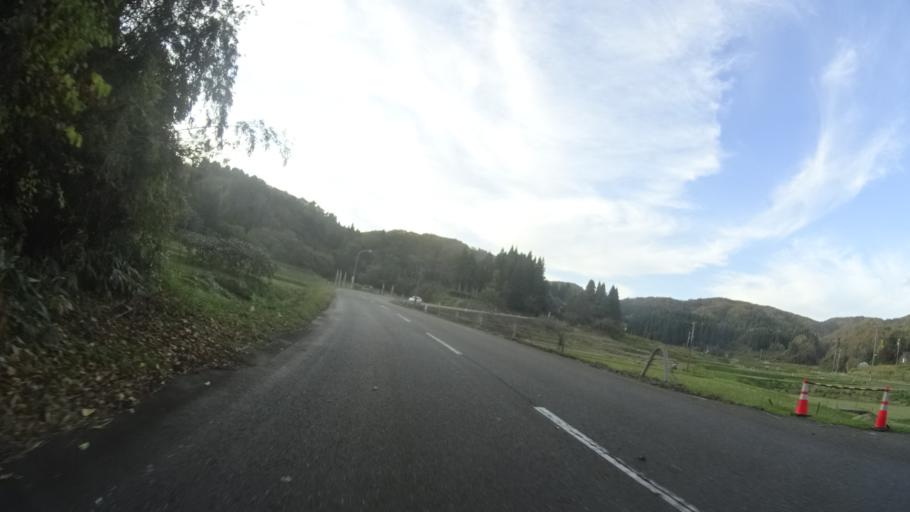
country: JP
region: Ishikawa
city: Nanao
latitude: 37.1949
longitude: 136.7151
